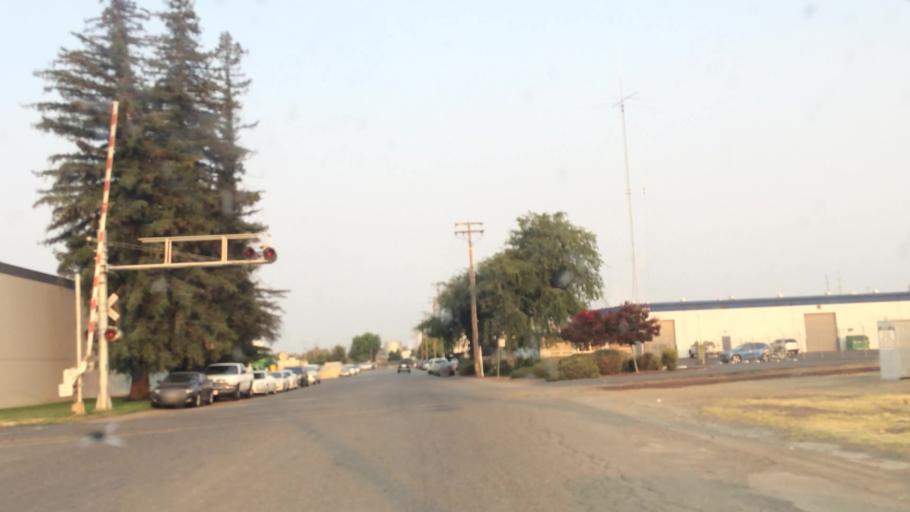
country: US
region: California
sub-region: Sacramento County
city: Rosemont
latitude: 38.5303
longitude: -121.3945
